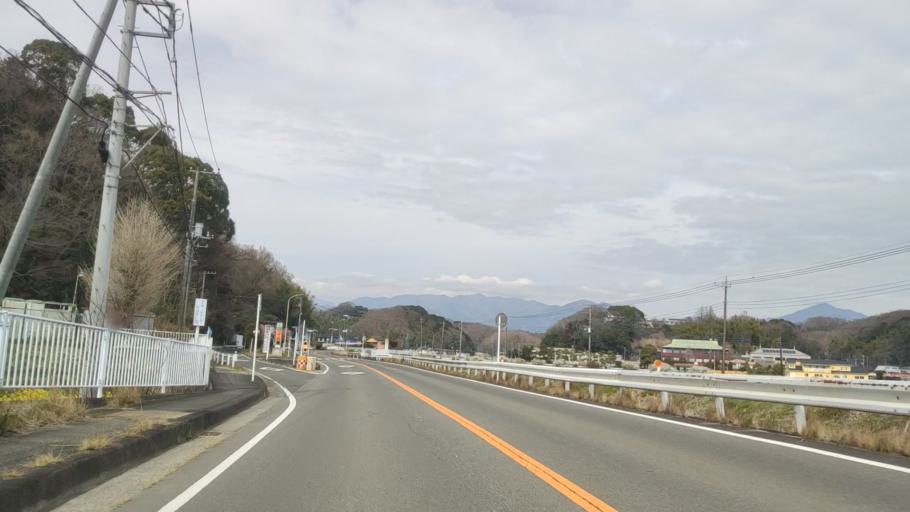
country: JP
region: Kanagawa
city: Ninomiya
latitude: 35.3270
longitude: 139.2192
